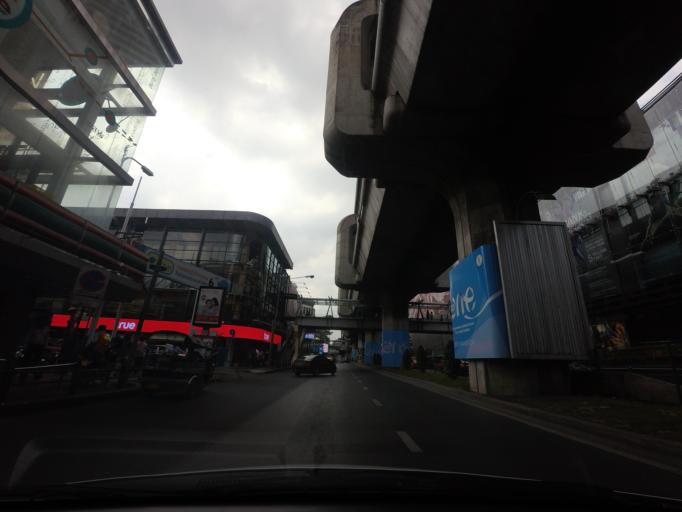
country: TH
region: Bangkok
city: Pathum Wan
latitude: 13.7459
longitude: 100.5324
